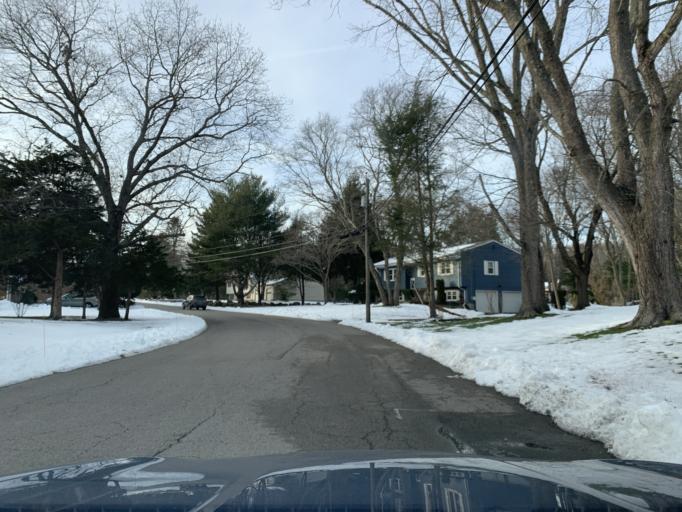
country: US
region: Rhode Island
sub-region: Washington County
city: North Kingstown
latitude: 41.5897
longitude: -71.4370
